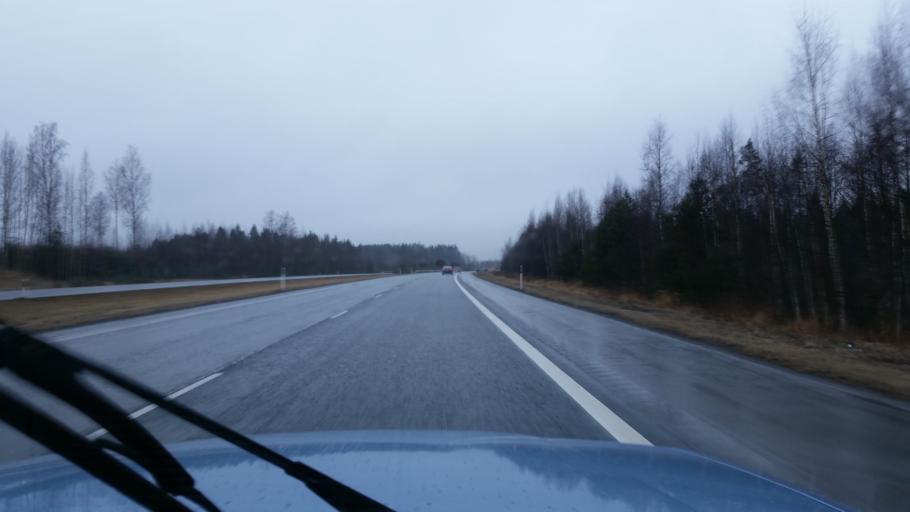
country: FI
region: Haeme
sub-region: Haemeenlinna
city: Kalvola
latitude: 61.0804
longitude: 24.2163
